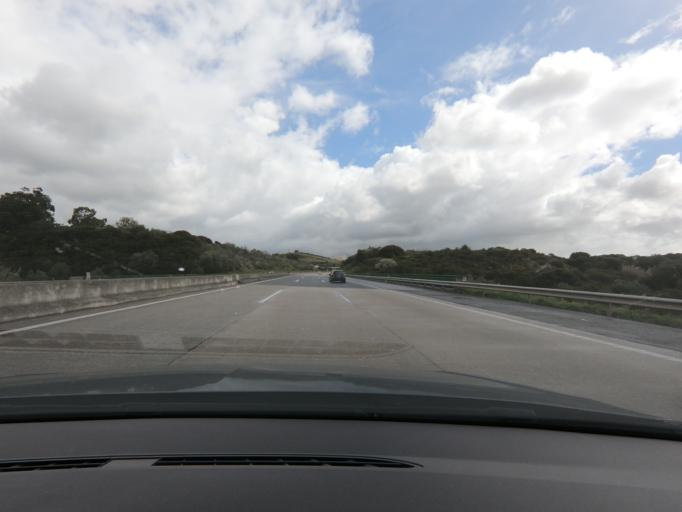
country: PT
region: Lisbon
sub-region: Loures
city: Santo Antao do Tojal
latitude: 38.8646
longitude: -9.1516
